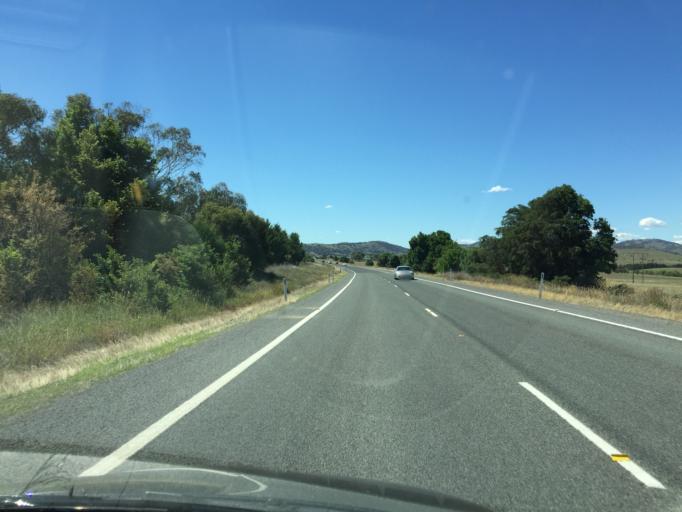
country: AU
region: Australian Capital Territory
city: Macarthur
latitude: -35.7328
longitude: 149.1607
